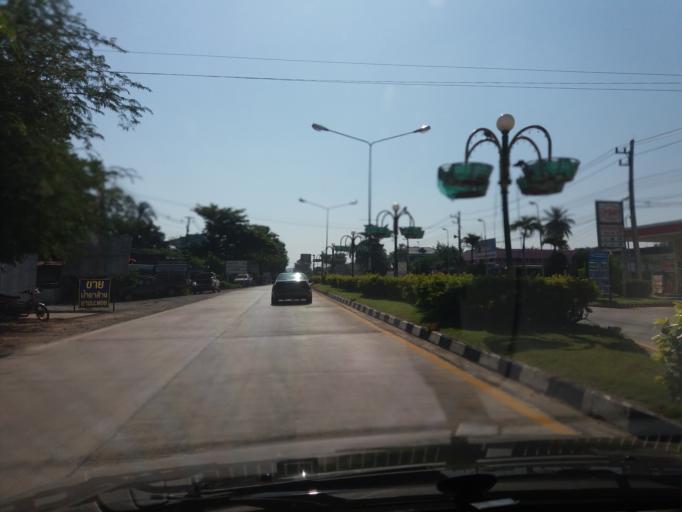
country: TH
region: Kamphaeng Phet
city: Khanu Woralaksaburi
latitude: 16.0701
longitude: 99.8633
